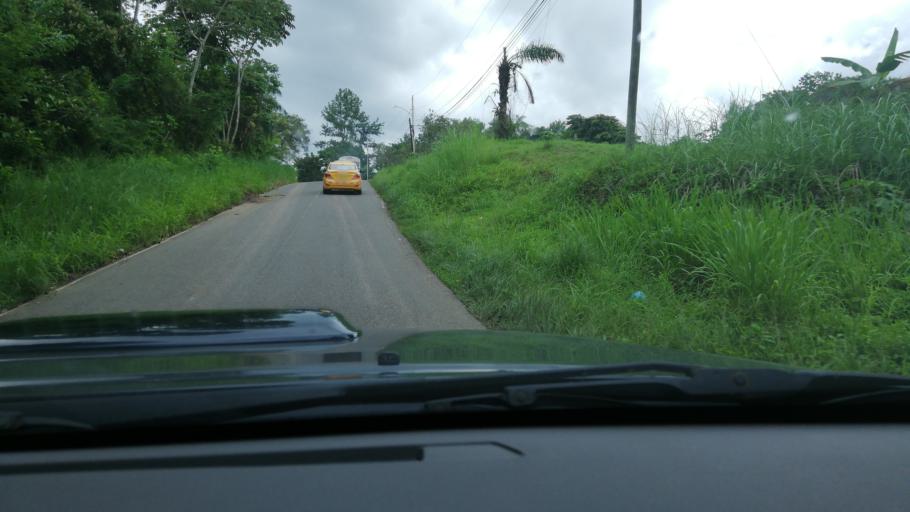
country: PA
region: Panama
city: San Miguelito
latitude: 9.0936
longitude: -79.4504
